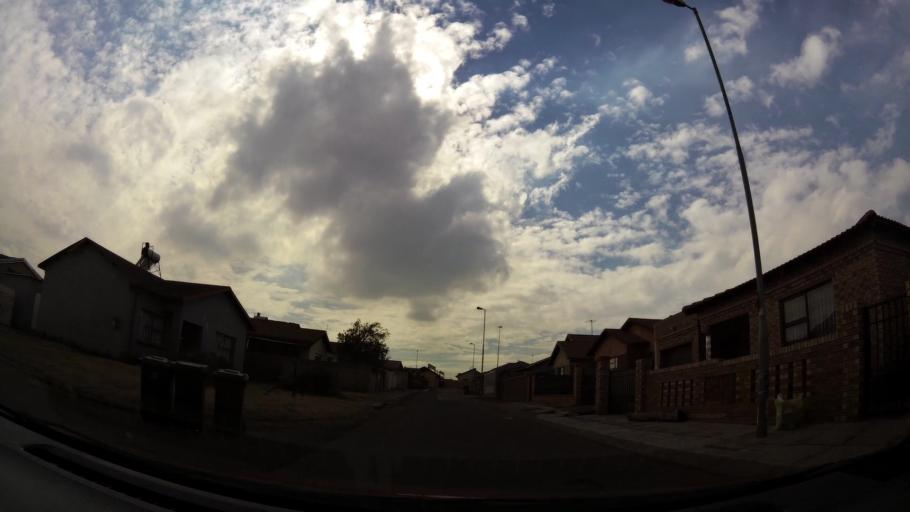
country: ZA
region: Gauteng
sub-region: City of Johannesburg Metropolitan Municipality
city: Soweto
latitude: -26.2551
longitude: 27.8154
